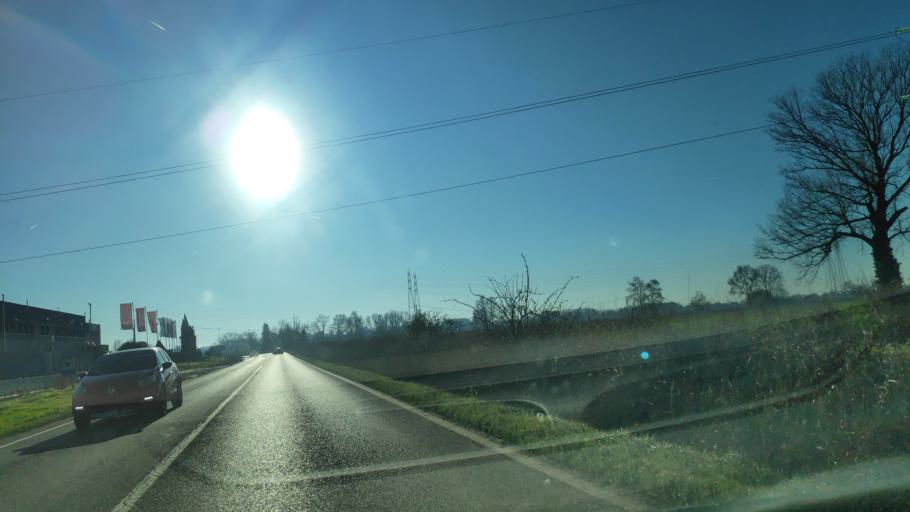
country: IT
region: Lombardy
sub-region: Citta metropolitana di Milano
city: Colturano
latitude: 45.3756
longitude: 9.3372
